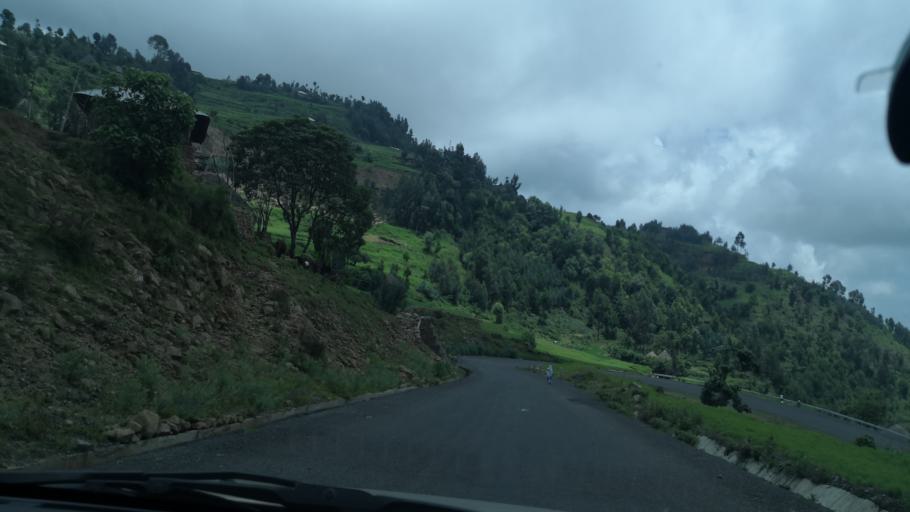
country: ET
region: Amhara
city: Abomsa
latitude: 10.3255
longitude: 39.8401
